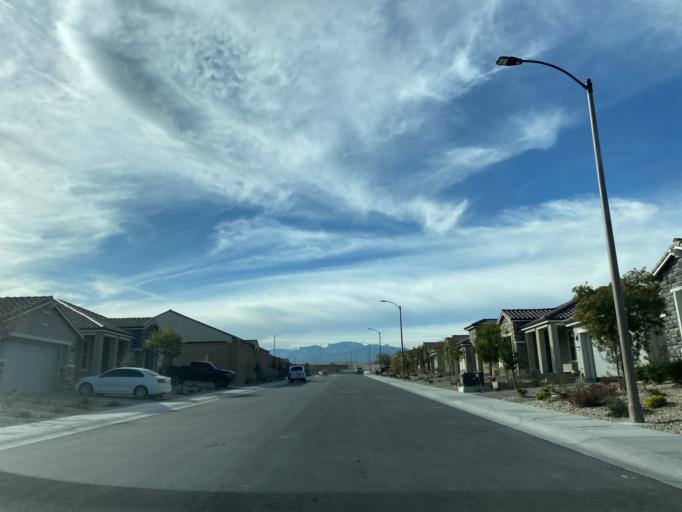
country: US
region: Nevada
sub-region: Clark County
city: Summerlin South
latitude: 36.3121
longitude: -115.3229
